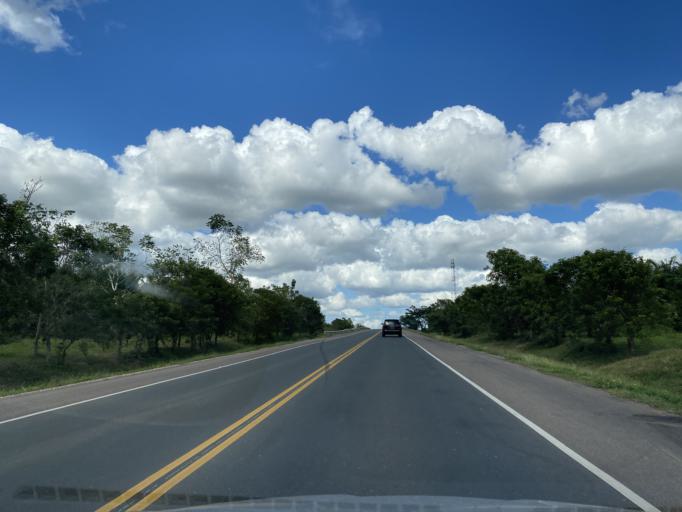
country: DO
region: Monte Plata
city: Monte Plata
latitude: 18.7251
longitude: -69.7607
